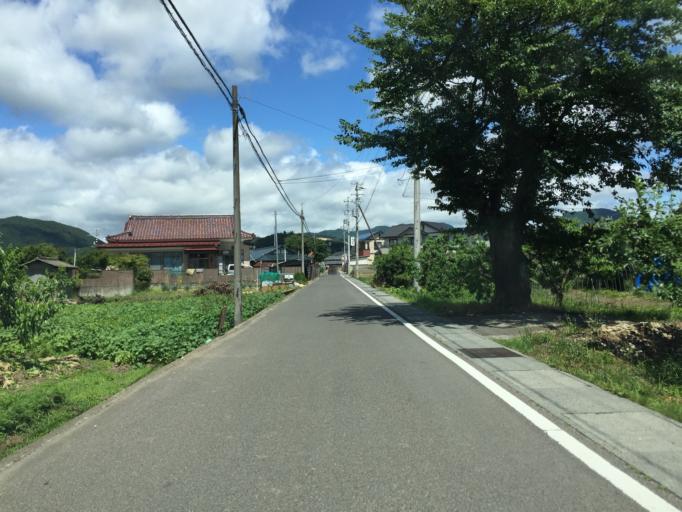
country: JP
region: Fukushima
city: Fukushima-shi
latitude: 37.8090
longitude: 140.4392
